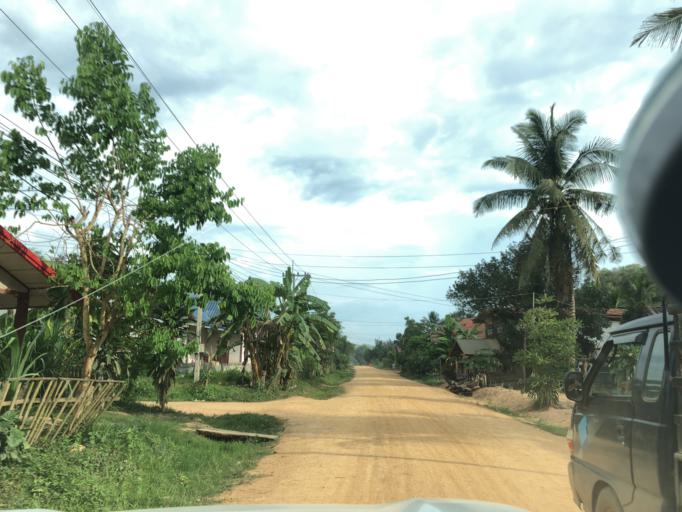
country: TH
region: Loei
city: Chiang Khan
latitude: 18.0159
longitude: 101.4193
